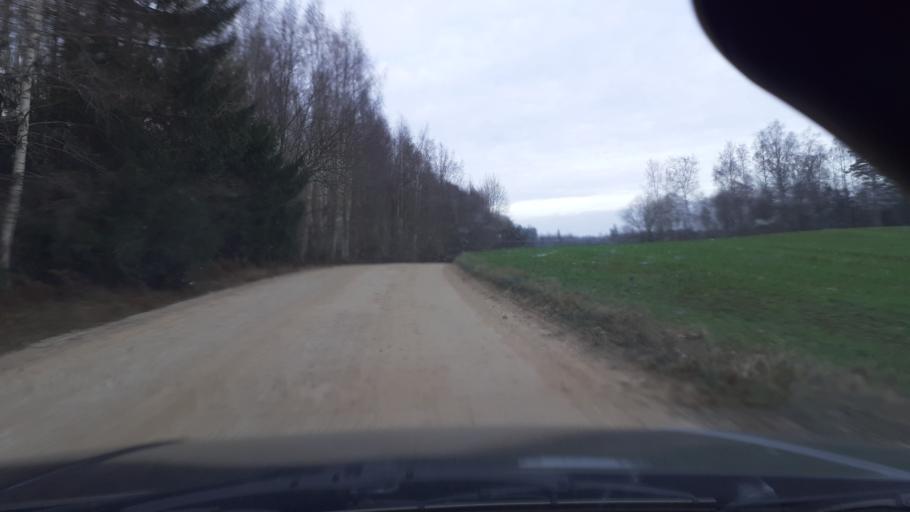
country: LV
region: Alsunga
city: Alsunga
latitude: 56.9581
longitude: 21.6503
